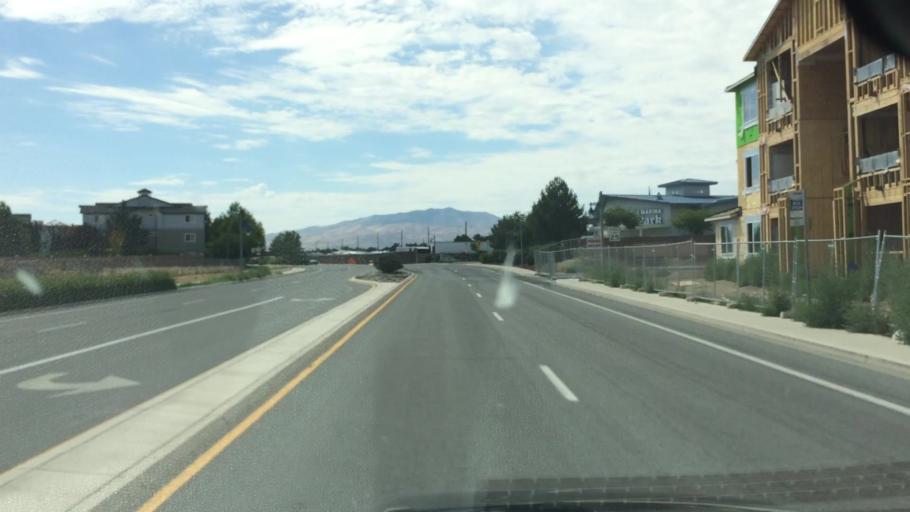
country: US
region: Nevada
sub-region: Washoe County
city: Sparks
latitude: 39.5370
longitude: -119.7230
